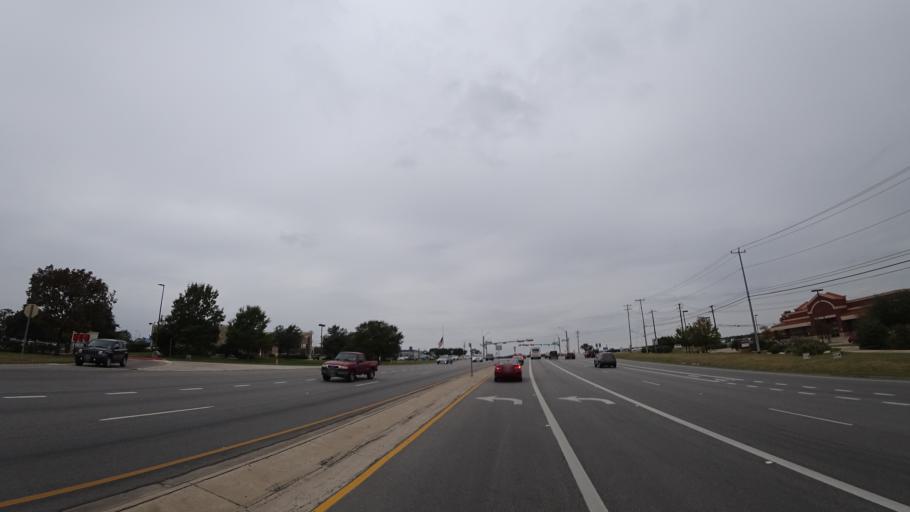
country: US
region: Texas
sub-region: Williamson County
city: Brushy Creek
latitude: 30.5332
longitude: -97.7821
